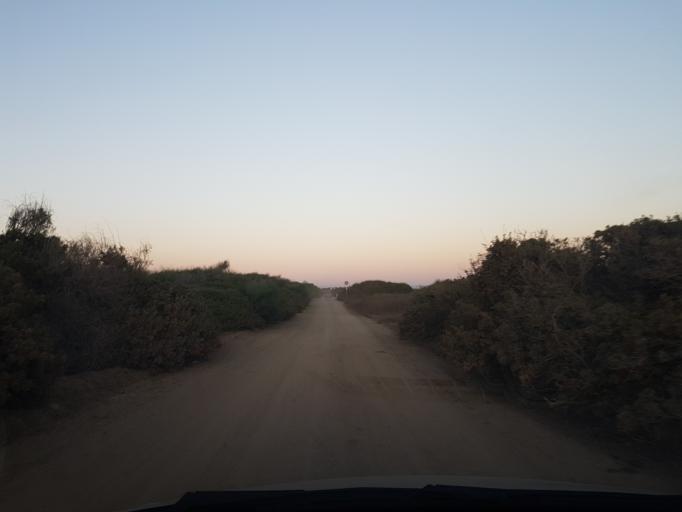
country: IT
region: Sardinia
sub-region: Provincia di Oristano
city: Riola Sardo
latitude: 40.0413
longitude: 8.3975
